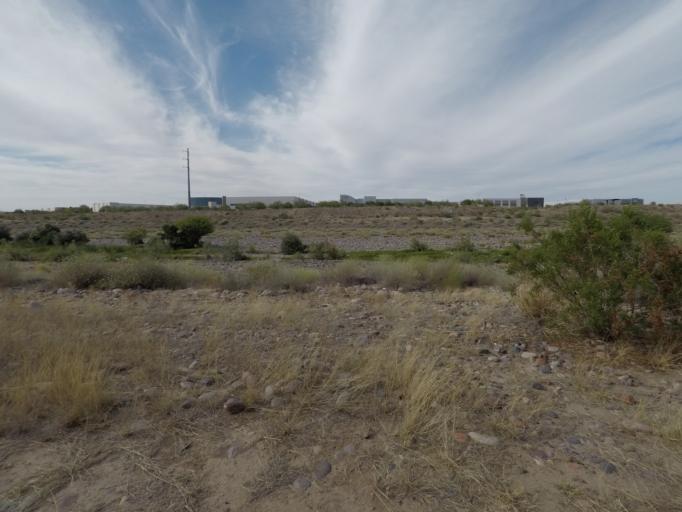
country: US
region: Arizona
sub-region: Maricopa County
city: Phoenix
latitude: 33.4162
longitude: -112.0427
